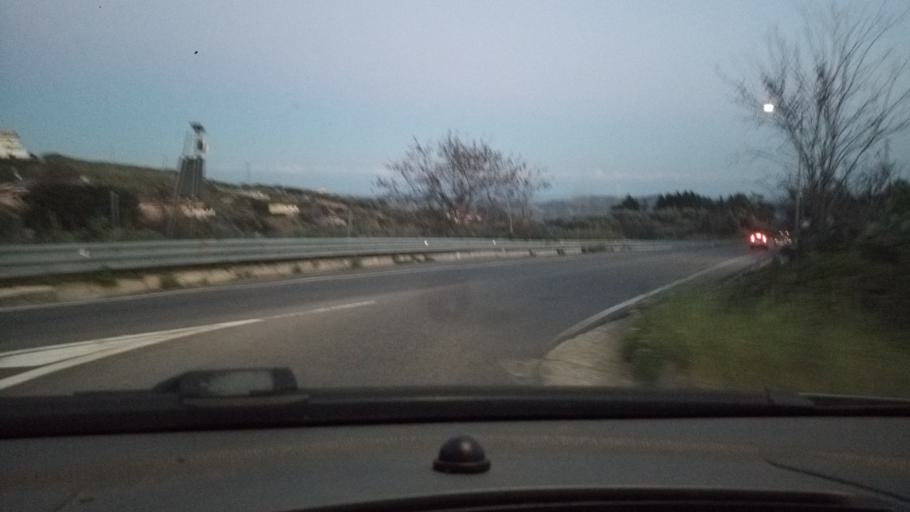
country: IT
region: Calabria
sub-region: Provincia di Catanzaro
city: Siano
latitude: 38.9078
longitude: 16.6027
